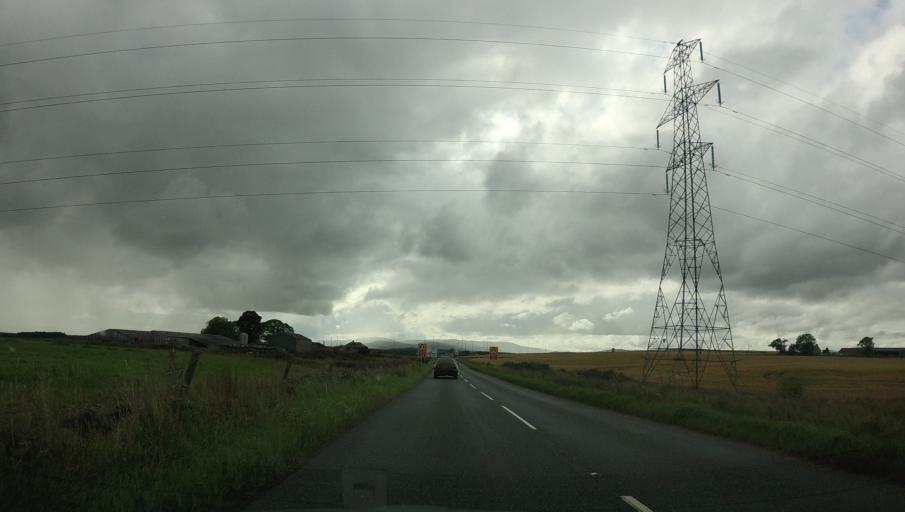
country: GB
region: Scotland
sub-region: Aberdeenshire
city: Westhill
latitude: 57.1432
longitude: -2.3048
